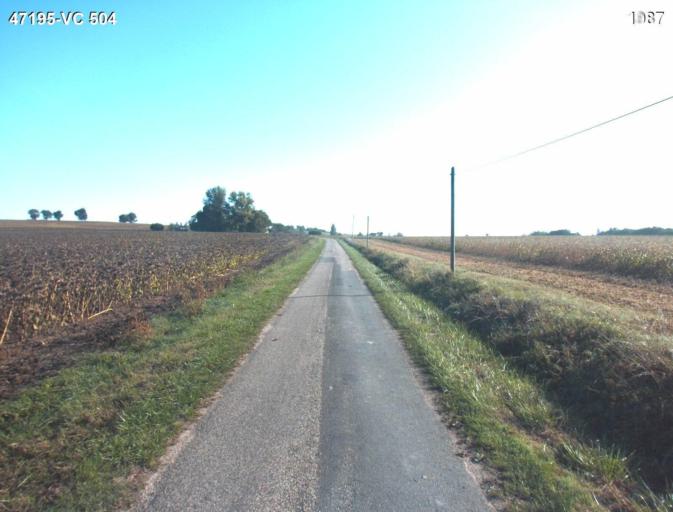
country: FR
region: Aquitaine
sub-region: Departement du Lot-et-Garonne
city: Nerac
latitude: 44.1639
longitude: 0.3362
